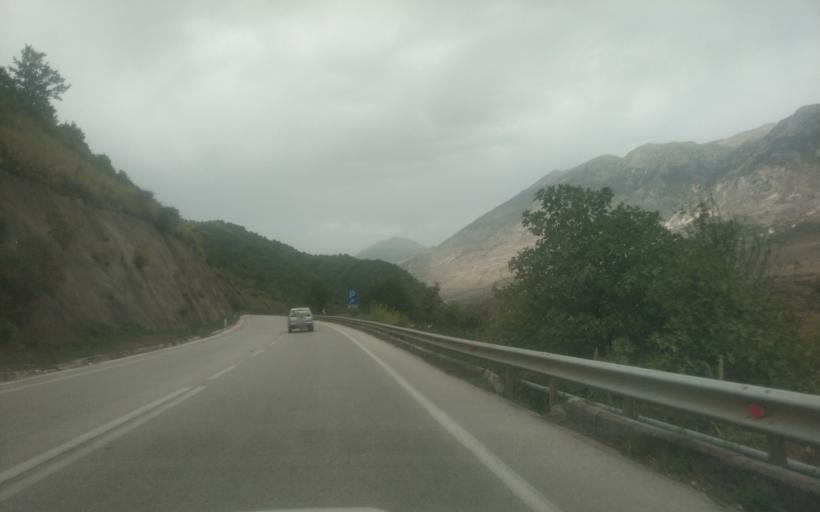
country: AL
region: Gjirokaster
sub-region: Rrethi i Gjirokastres
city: Picar
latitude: 40.2121
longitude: 20.0880
